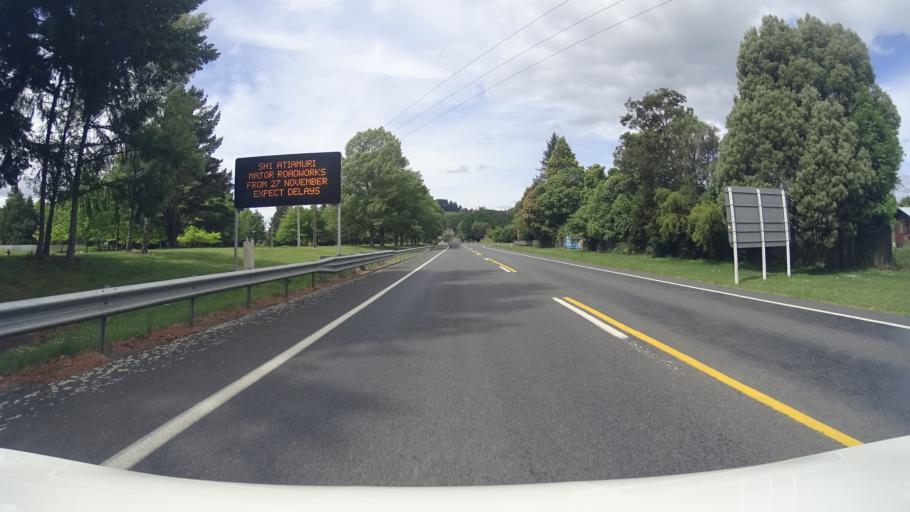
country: NZ
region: Waikato
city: Turangi
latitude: -38.9892
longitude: 175.8137
